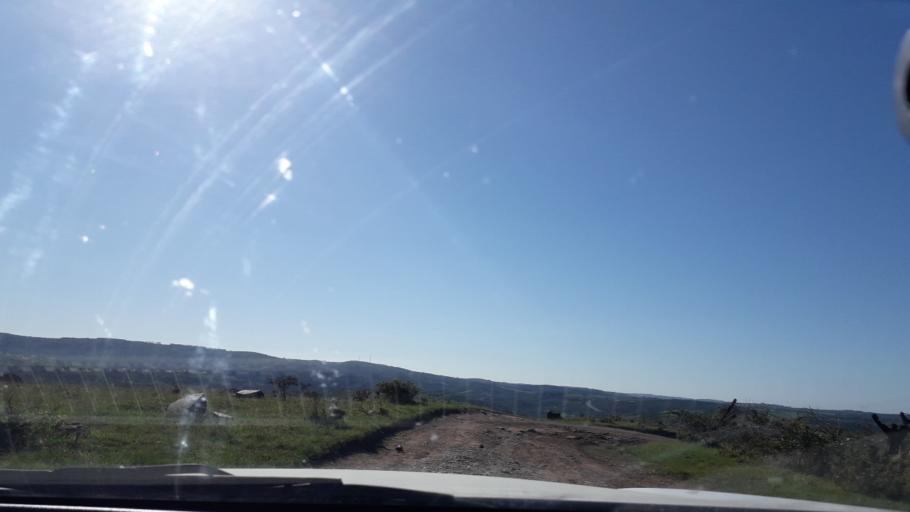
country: ZA
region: Eastern Cape
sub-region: Buffalo City Metropolitan Municipality
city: East London
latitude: -32.8412
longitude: 27.9837
